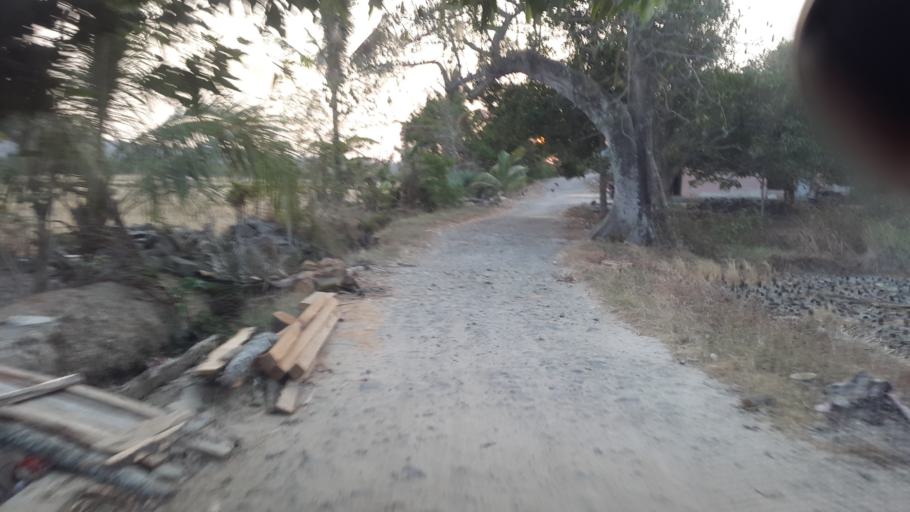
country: ID
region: West Java
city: Ciwaru
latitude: -7.2153
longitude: 106.4974
